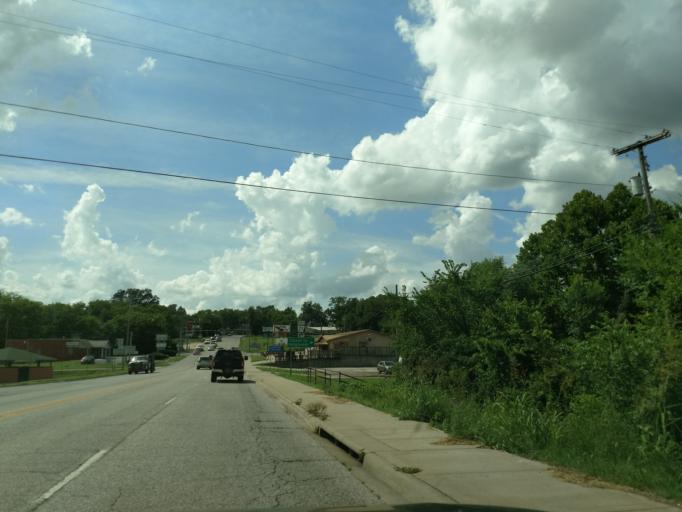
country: US
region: Arkansas
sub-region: Carroll County
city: Berryville
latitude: 36.3599
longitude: -93.5626
